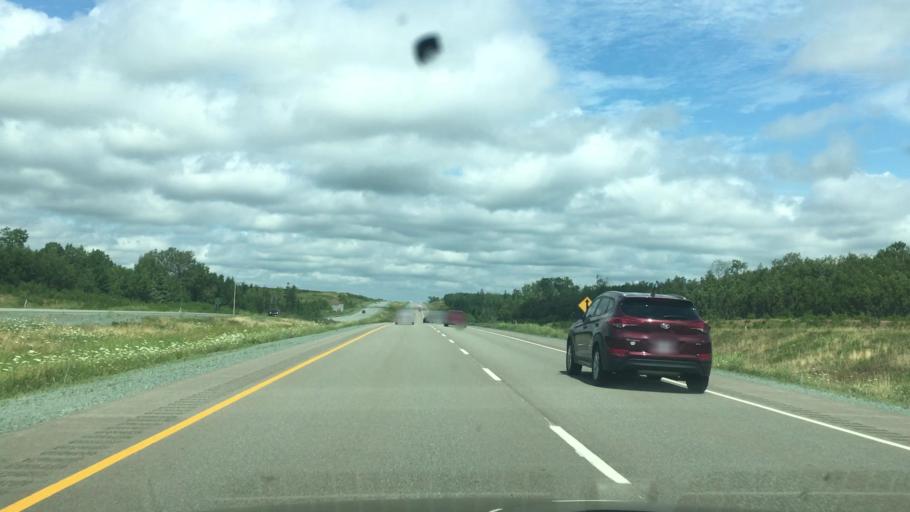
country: CA
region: Nova Scotia
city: Oxford
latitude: 45.6093
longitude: -63.7365
